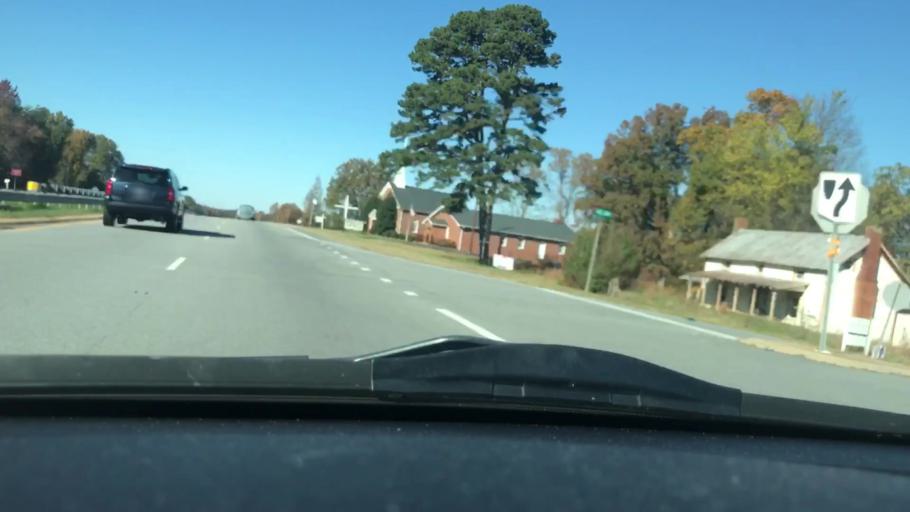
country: US
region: North Carolina
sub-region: Rockingham County
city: Madison
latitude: 36.3133
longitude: -79.9423
